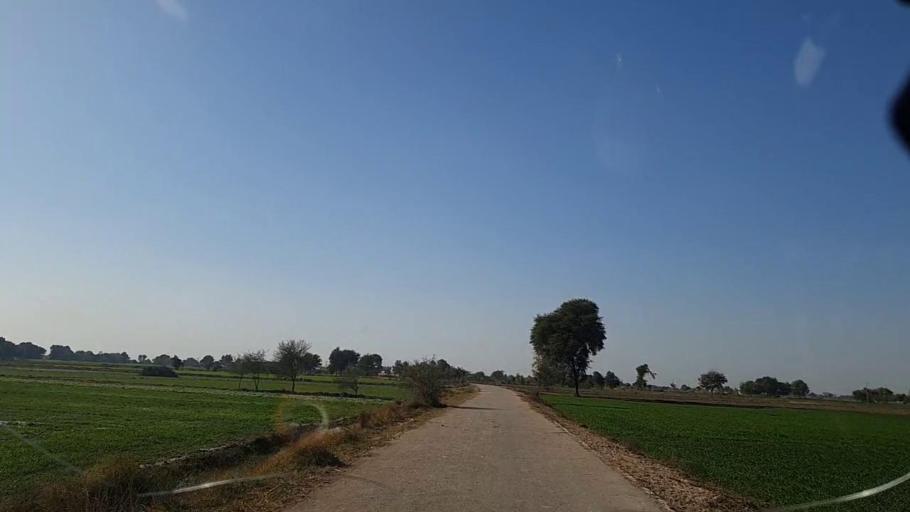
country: PK
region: Sindh
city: Khanpur
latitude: 27.7778
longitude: 69.3610
